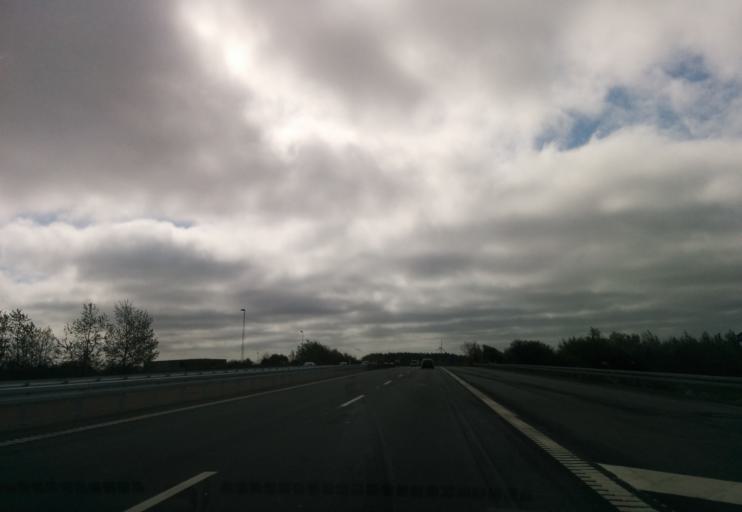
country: DK
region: South Denmark
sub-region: Middelfart Kommune
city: Norre Aby
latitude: 55.4713
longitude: 9.8940
